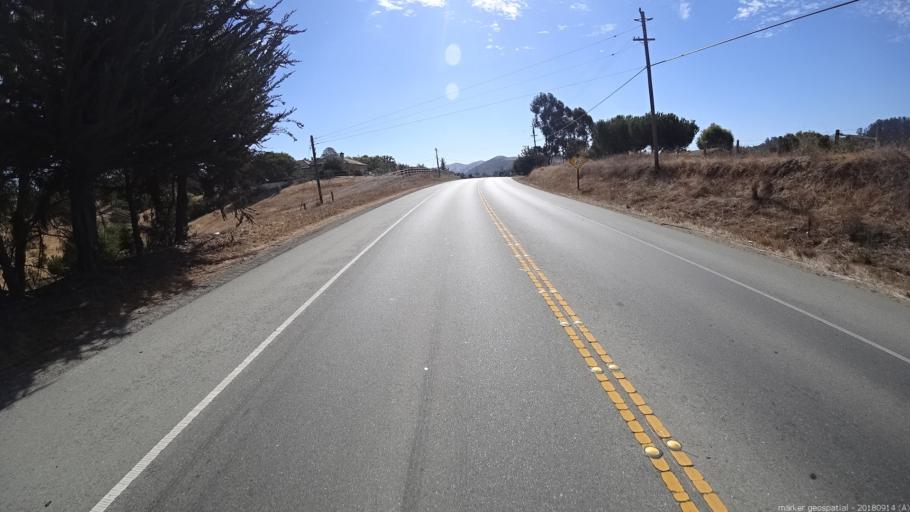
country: US
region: California
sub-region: San Benito County
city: Aromas
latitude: 36.8568
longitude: -121.6428
